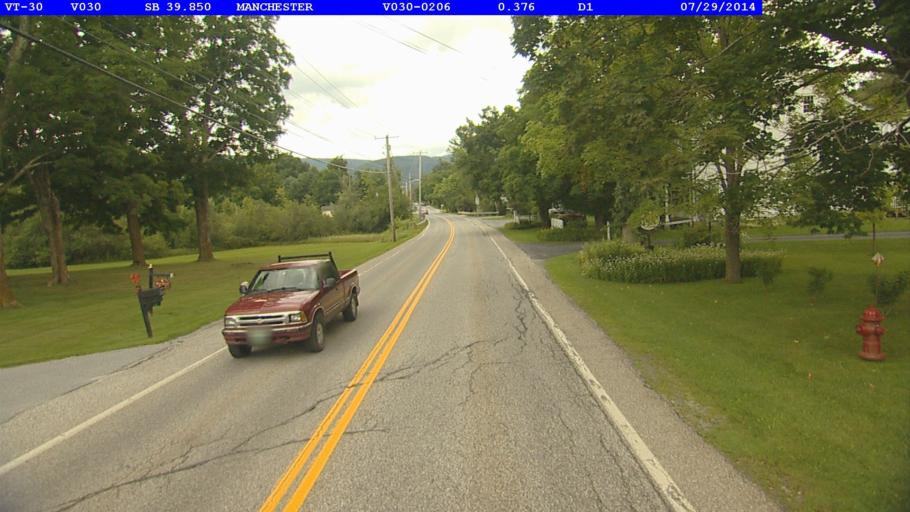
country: US
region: Vermont
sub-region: Bennington County
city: Manchester Center
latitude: 43.1821
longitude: -73.0579
